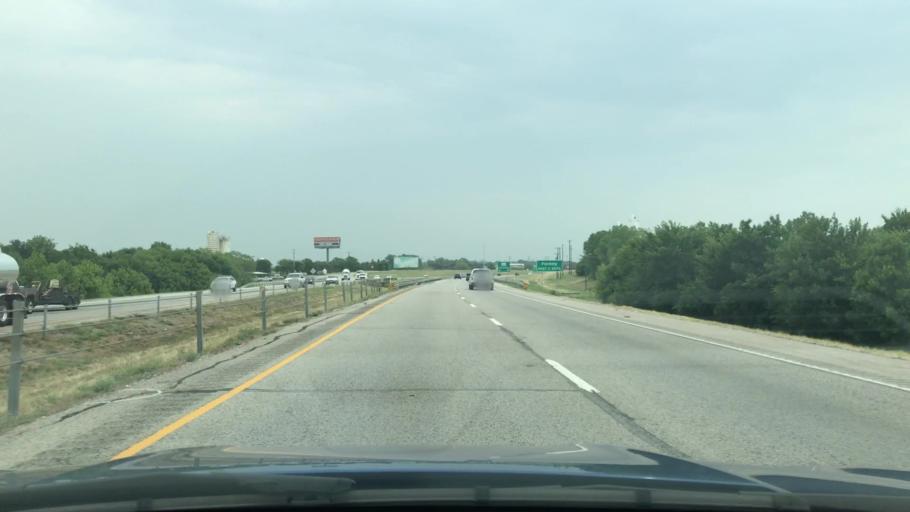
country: US
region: Texas
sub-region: Kaufman County
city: Forney
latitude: 32.7730
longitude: -96.4963
